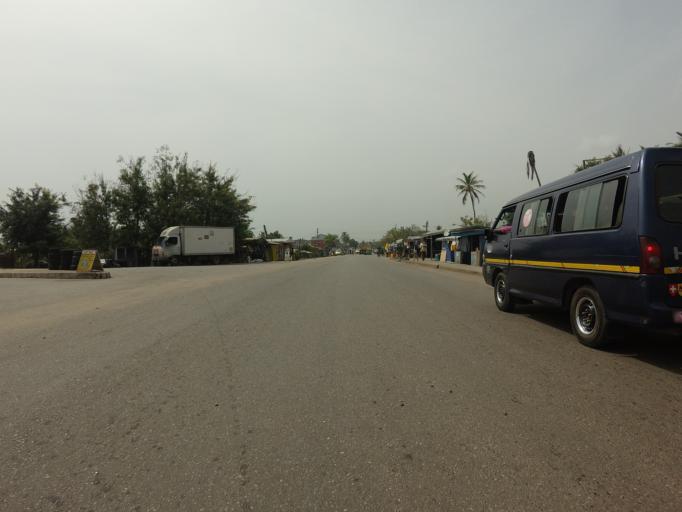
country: GH
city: Akropong
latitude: 6.1539
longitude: 0.0602
